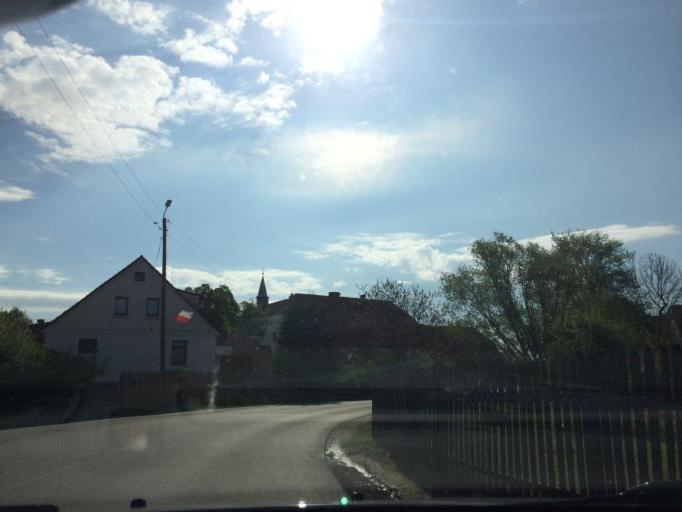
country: PL
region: Lower Silesian Voivodeship
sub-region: Powiat dzierzoniowski
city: Pieszyce
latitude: 50.7574
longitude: 16.5369
